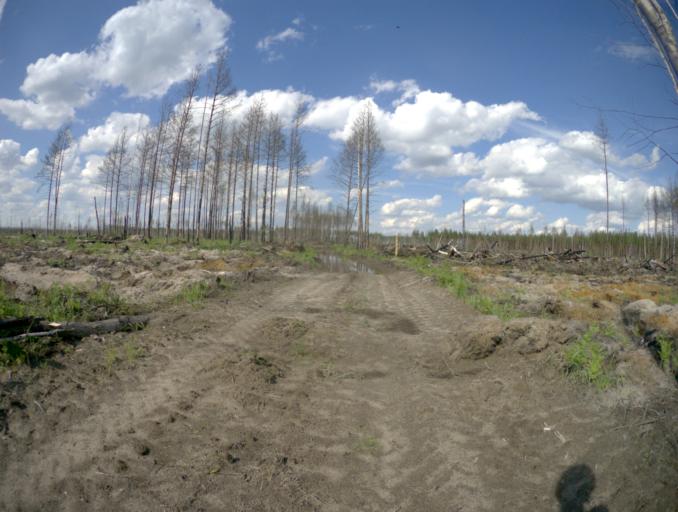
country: RU
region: Vladimir
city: Velikodvorskiy
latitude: 55.3146
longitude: 40.9181
